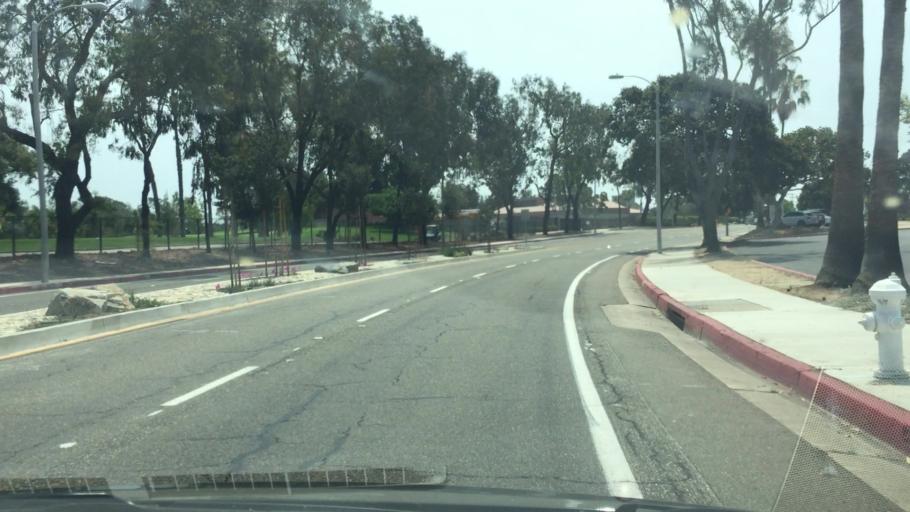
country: US
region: California
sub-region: Orange County
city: Costa Mesa
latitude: 33.6606
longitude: -117.9347
